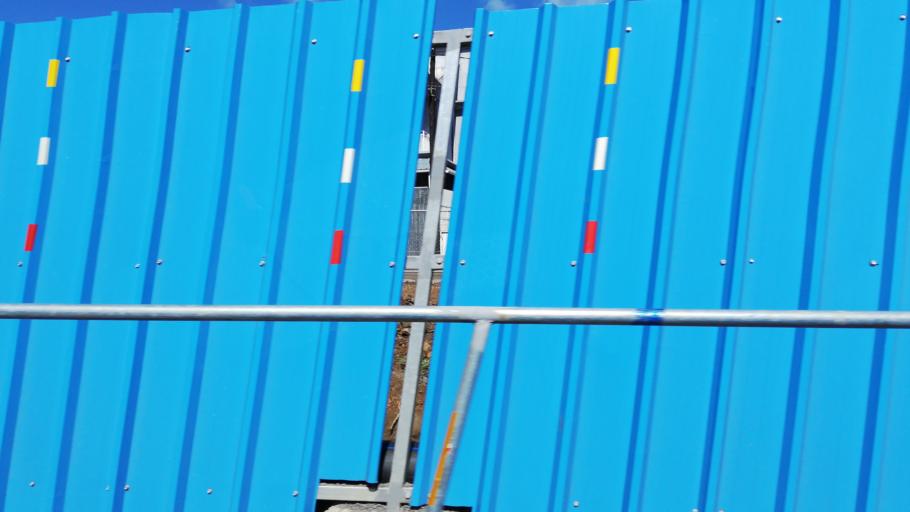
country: MU
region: Plaines Wilhems
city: Ebene
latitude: -20.2364
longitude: 57.4740
